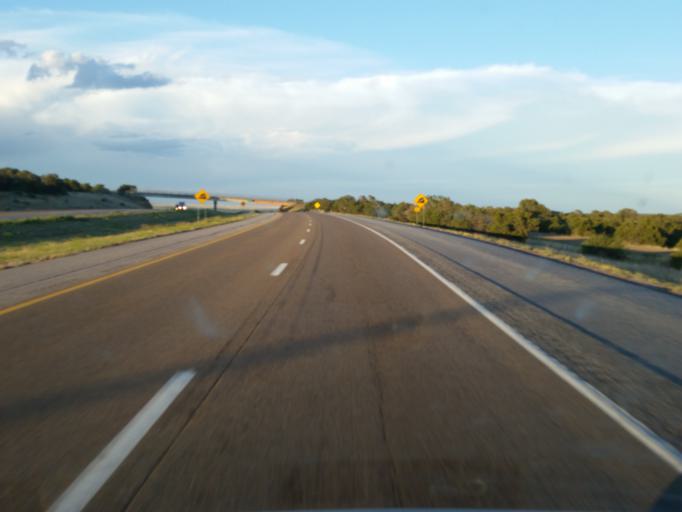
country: US
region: New Mexico
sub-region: Torrance County
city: Moriarty
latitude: 35.0024
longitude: -105.5497
